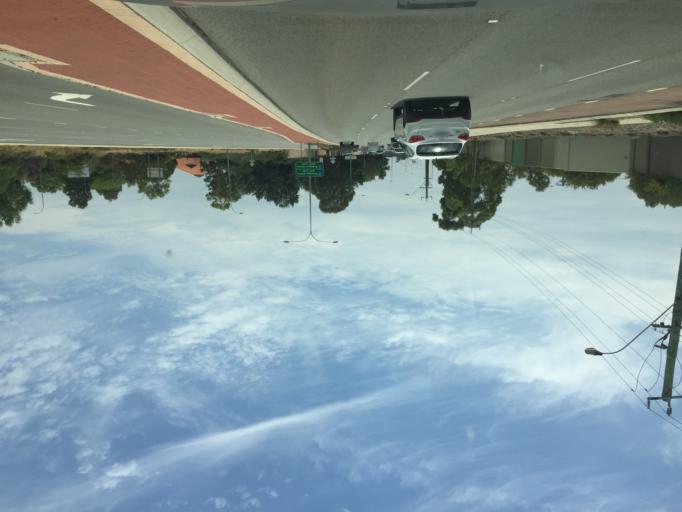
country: AU
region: Western Australia
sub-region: Melville
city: Winthrop
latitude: -32.0655
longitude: 115.8435
